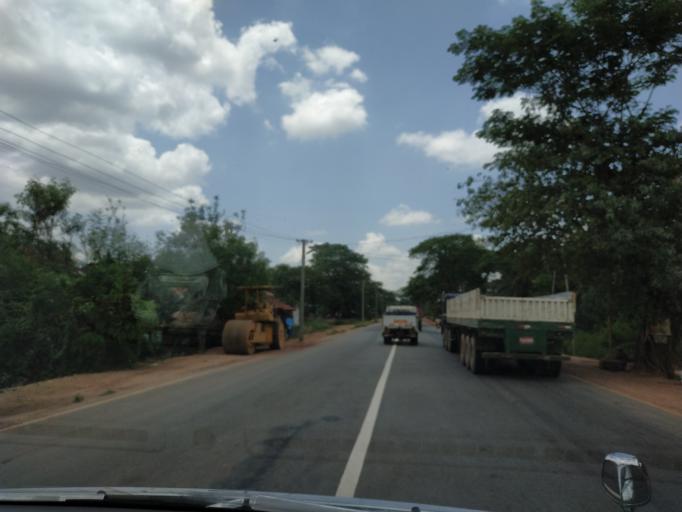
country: MM
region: Bago
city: Bago
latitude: 17.4672
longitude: 96.5806
